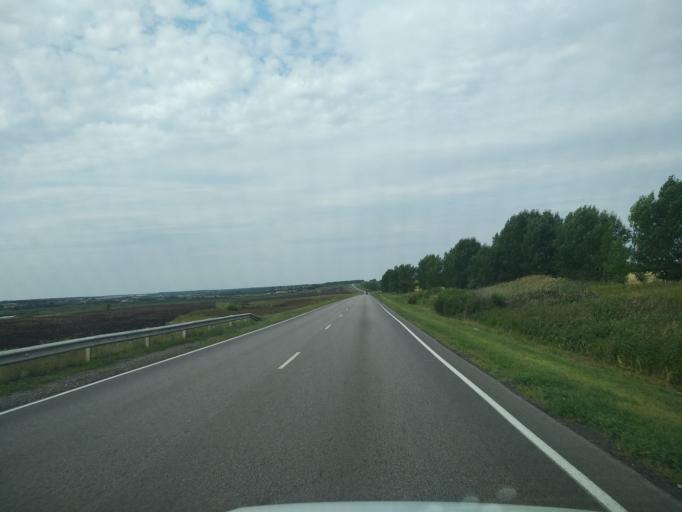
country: RU
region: Voronezj
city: Pereleshinskiy
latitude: 51.8605
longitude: 40.3544
